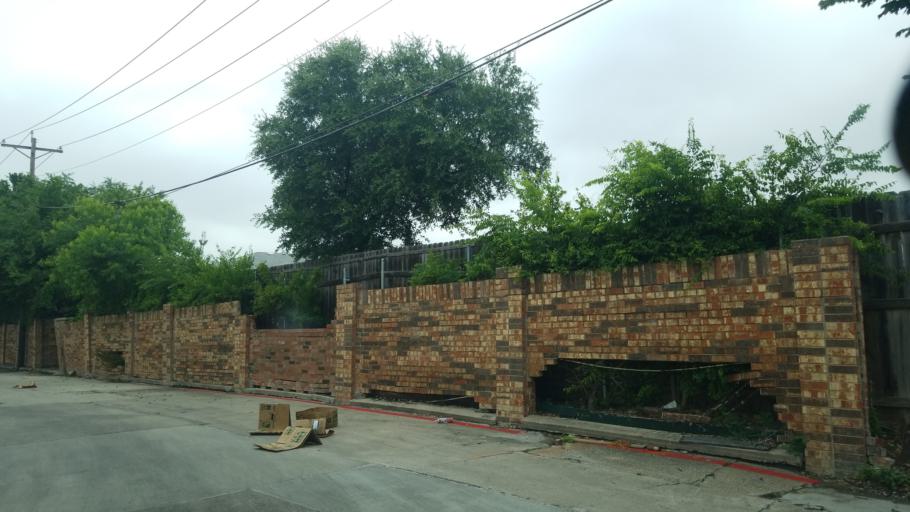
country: US
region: Texas
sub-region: Dallas County
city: Farmers Branch
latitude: 32.9083
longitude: -96.8694
